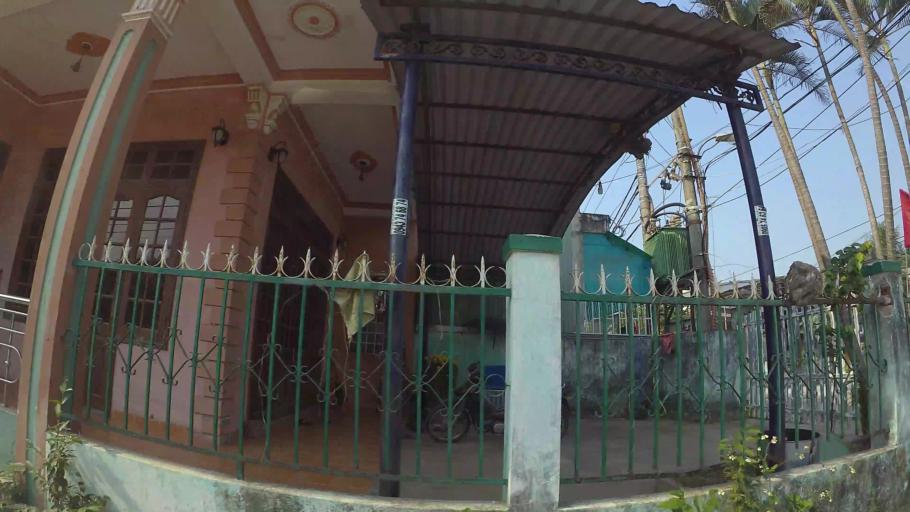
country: VN
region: Da Nang
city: Cam Le
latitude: 16.0159
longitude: 108.1865
